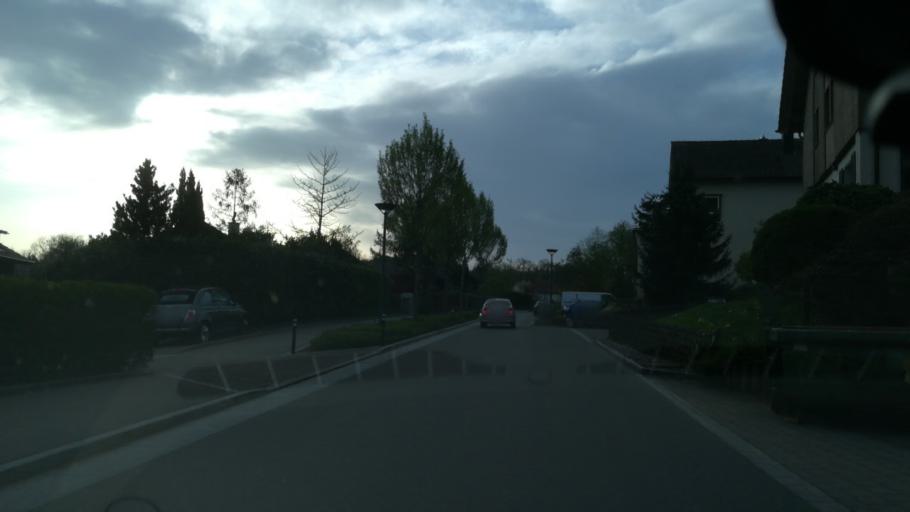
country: CH
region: Zurich
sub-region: Bezirk Uster
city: Gockhausen
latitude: 47.3782
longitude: 8.6042
